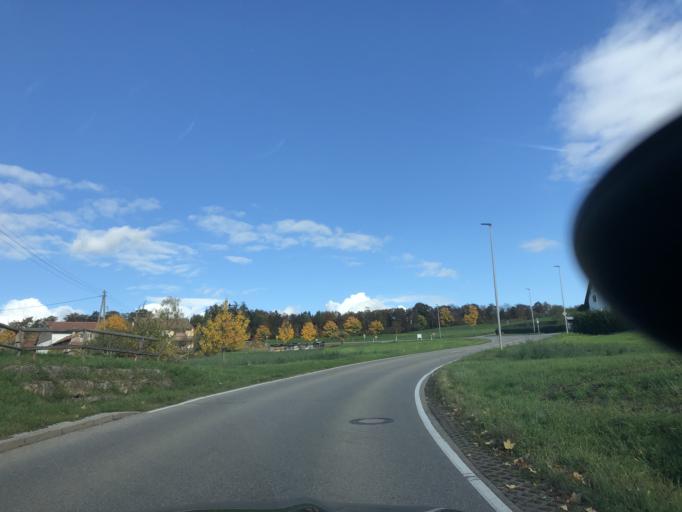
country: DE
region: Baden-Wuerttemberg
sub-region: Regierungsbezirk Stuttgart
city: Allmersbach im Tal
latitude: 48.8882
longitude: 9.4602
